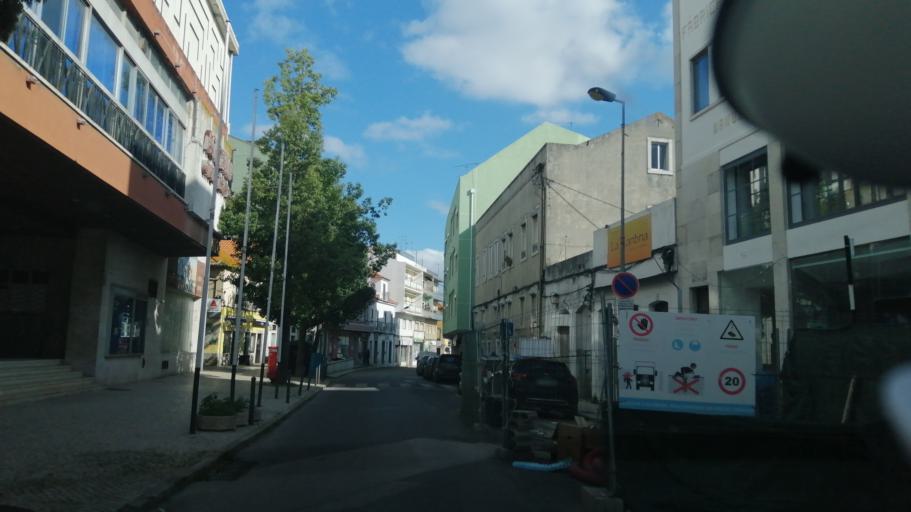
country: PT
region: Setubal
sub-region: Almada
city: Almada
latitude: 38.6804
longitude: -9.1601
